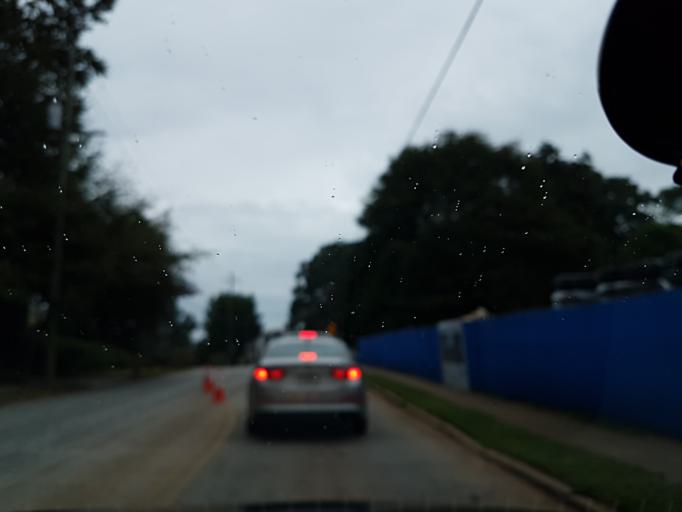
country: US
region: Georgia
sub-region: DeKalb County
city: Decatur
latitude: 33.7687
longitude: -84.2964
